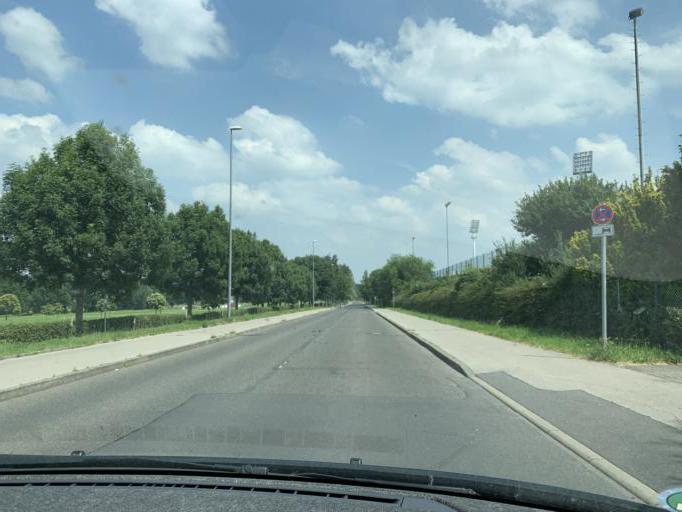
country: DE
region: North Rhine-Westphalia
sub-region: Regierungsbezirk Koln
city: Aachen
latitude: 50.7941
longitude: 6.0910
